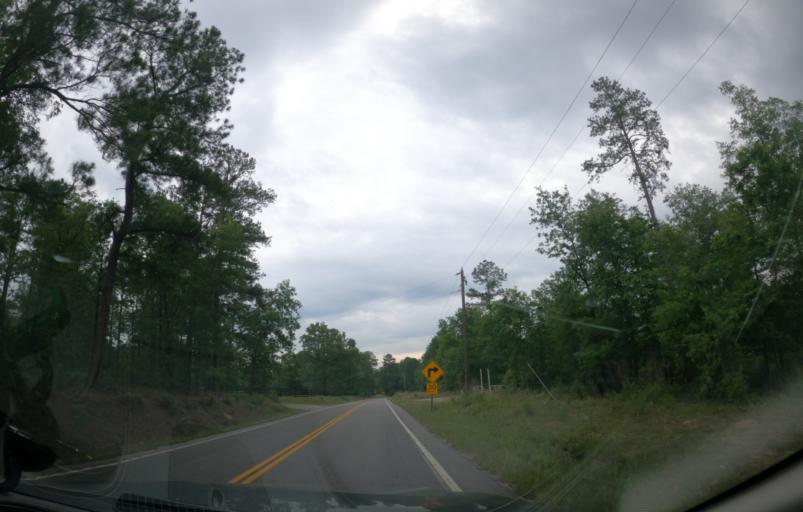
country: US
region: South Carolina
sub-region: Aiken County
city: Aiken
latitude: 33.5760
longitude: -81.6326
